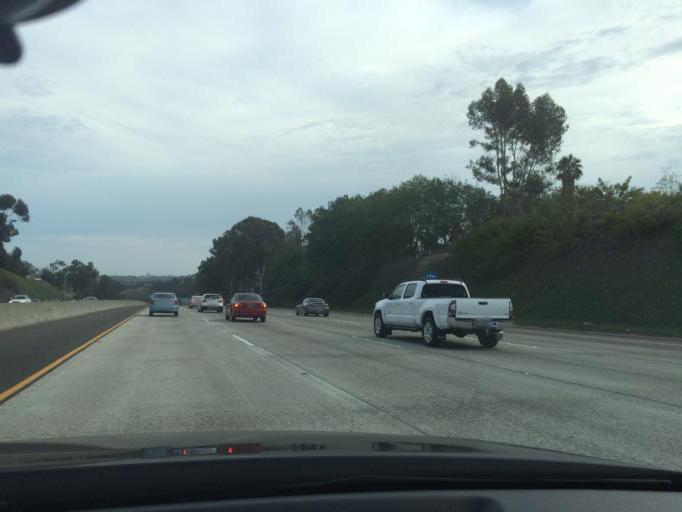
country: US
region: California
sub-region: San Diego County
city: San Diego
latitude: 32.7875
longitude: -117.1604
